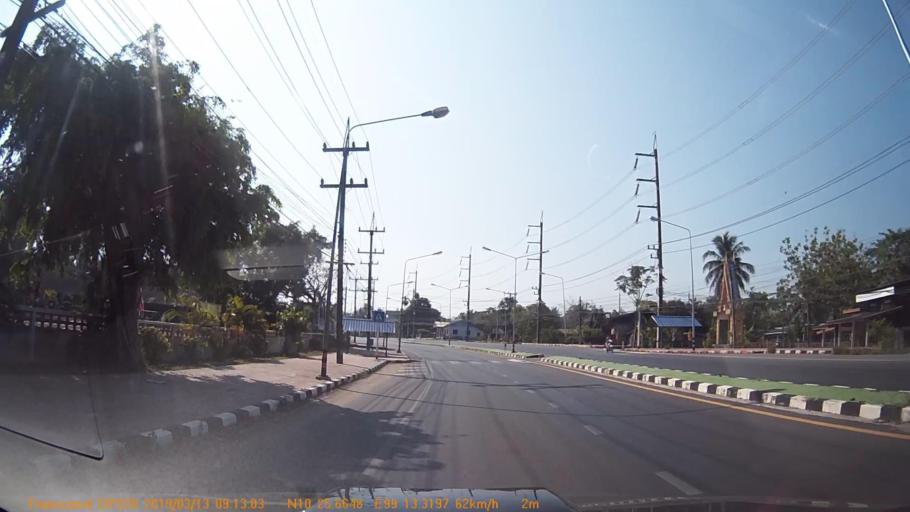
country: TH
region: Chumphon
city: Chumphon
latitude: 10.4275
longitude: 99.2221
